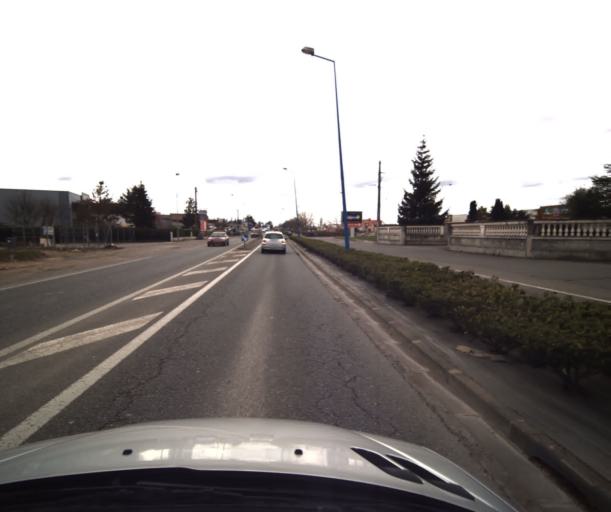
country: FR
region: Midi-Pyrenees
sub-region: Departement du Tarn-et-Garonne
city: Montauban
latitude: 44.0427
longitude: 1.3869
